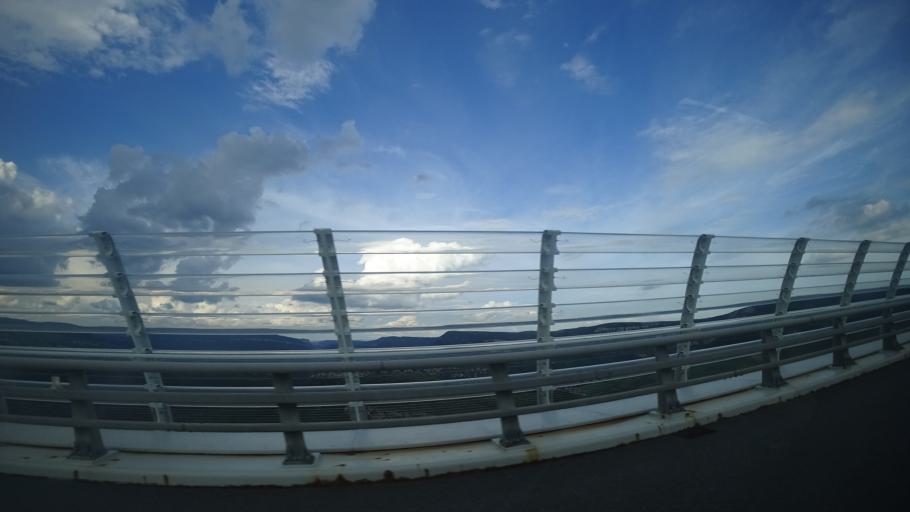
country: FR
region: Midi-Pyrenees
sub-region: Departement de l'Aveyron
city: Creissels
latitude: 44.0865
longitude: 3.0218
